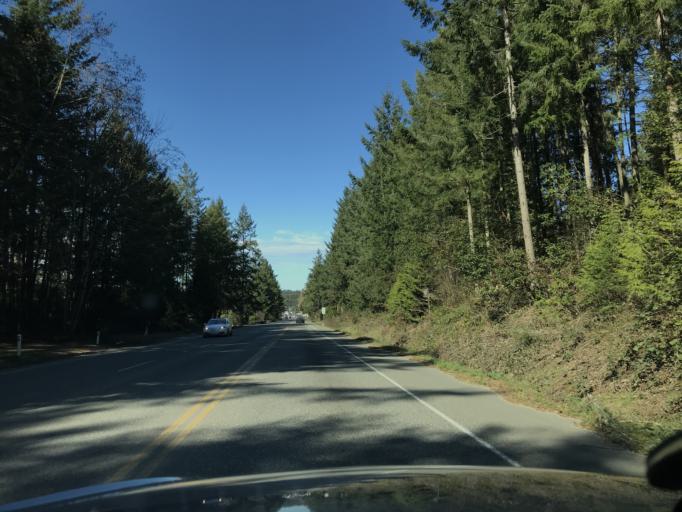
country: US
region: Washington
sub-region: Pierce County
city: Purdy
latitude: 47.3780
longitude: -122.6234
